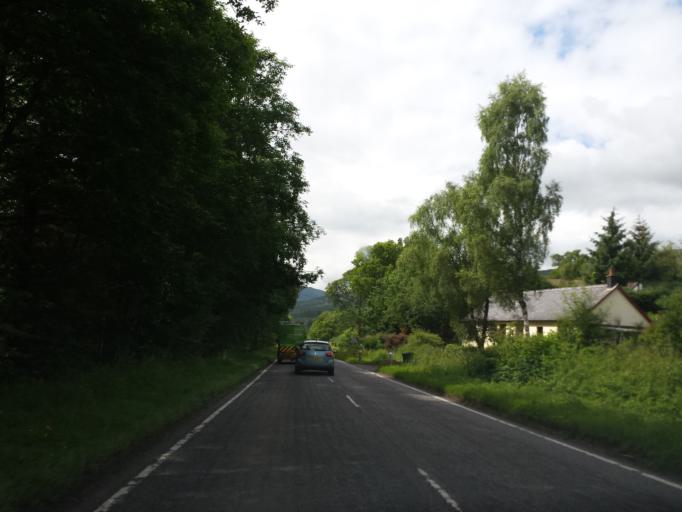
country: GB
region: Scotland
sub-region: Highland
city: Fort William
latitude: 56.8483
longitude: -5.1620
